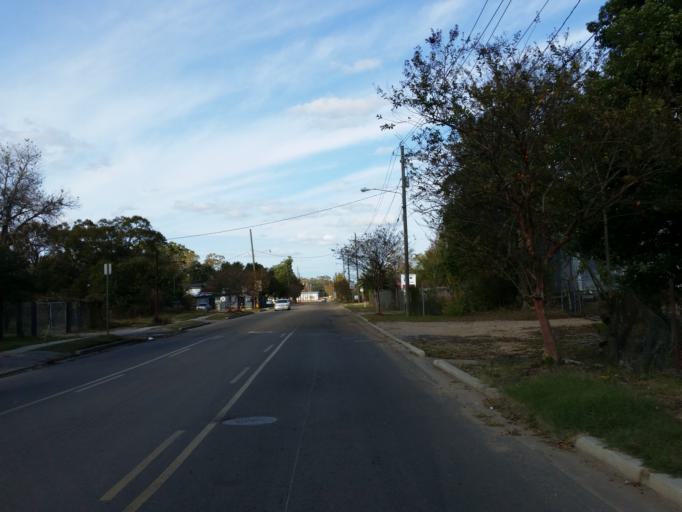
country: US
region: Mississippi
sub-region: Forrest County
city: Hattiesburg
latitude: 31.3361
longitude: -89.2872
